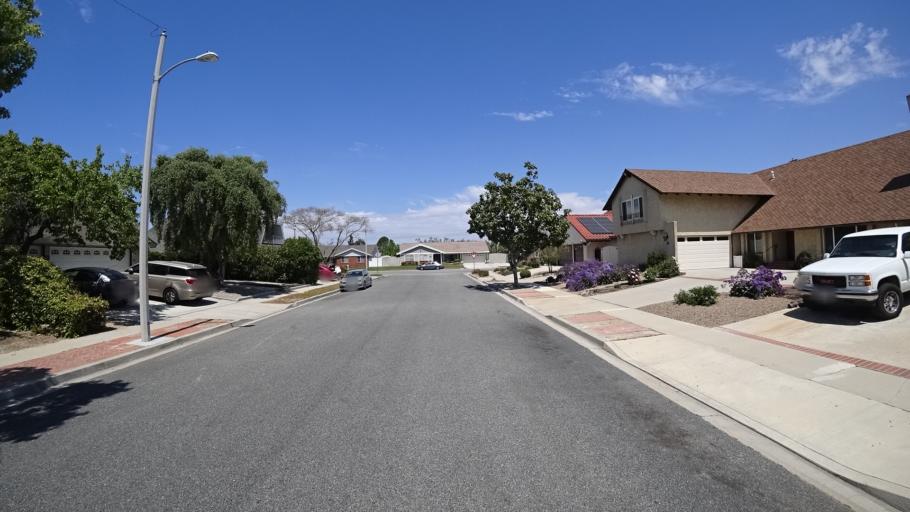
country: US
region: California
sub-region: Ventura County
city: Casa Conejo
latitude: 34.1782
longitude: -118.9194
